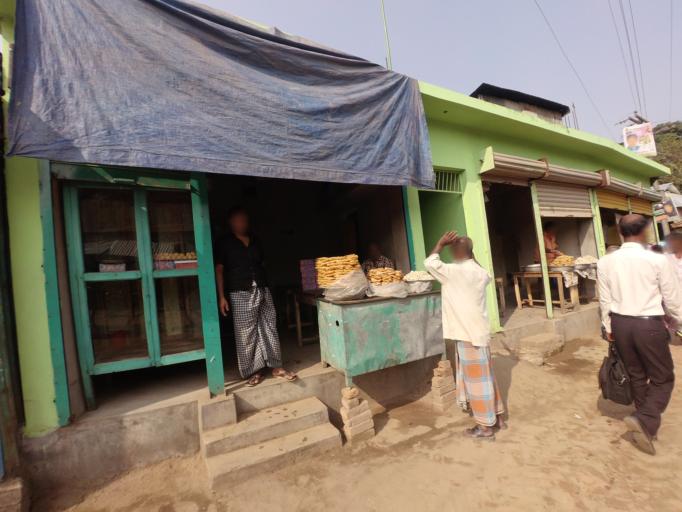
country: BD
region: Dhaka
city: Netrakona
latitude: 25.0102
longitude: 90.6487
